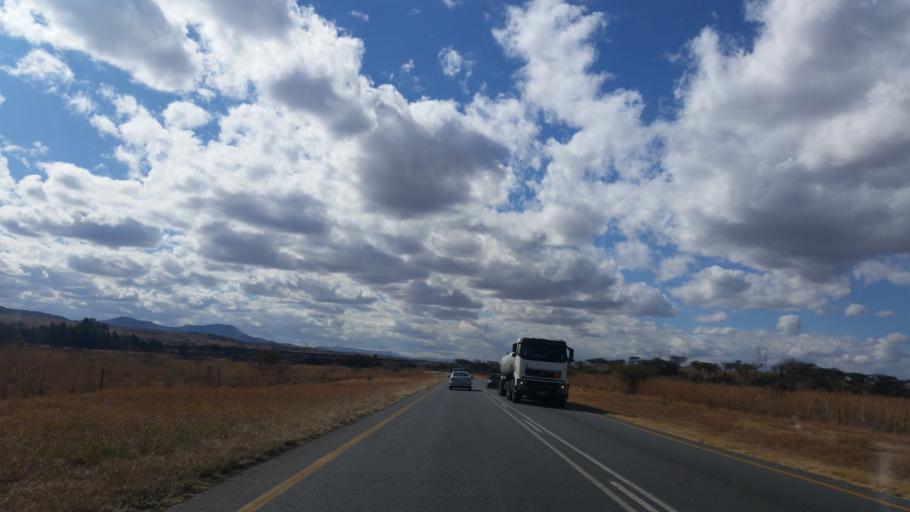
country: ZA
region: KwaZulu-Natal
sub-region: uThukela District Municipality
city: Ladysmith
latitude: -28.4993
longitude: 29.8363
